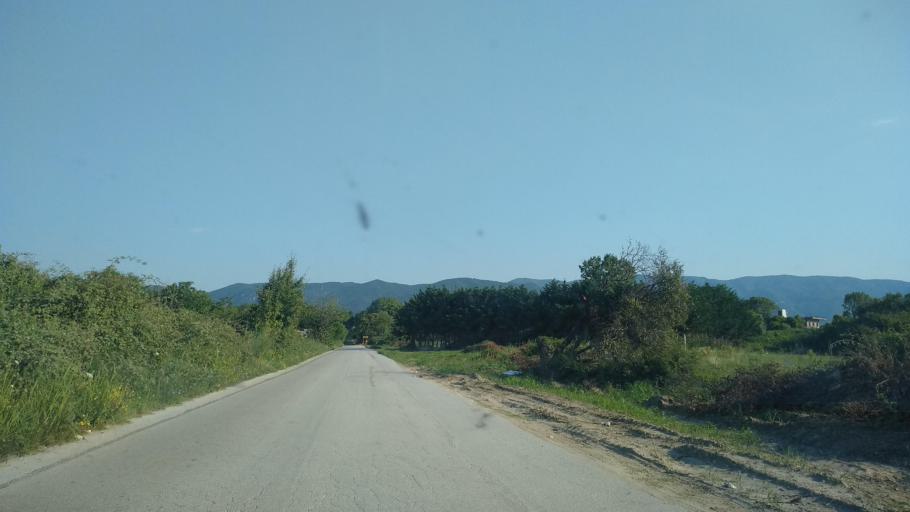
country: GR
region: Central Macedonia
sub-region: Nomos Thessalonikis
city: Stavros
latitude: 40.6733
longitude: 23.6903
